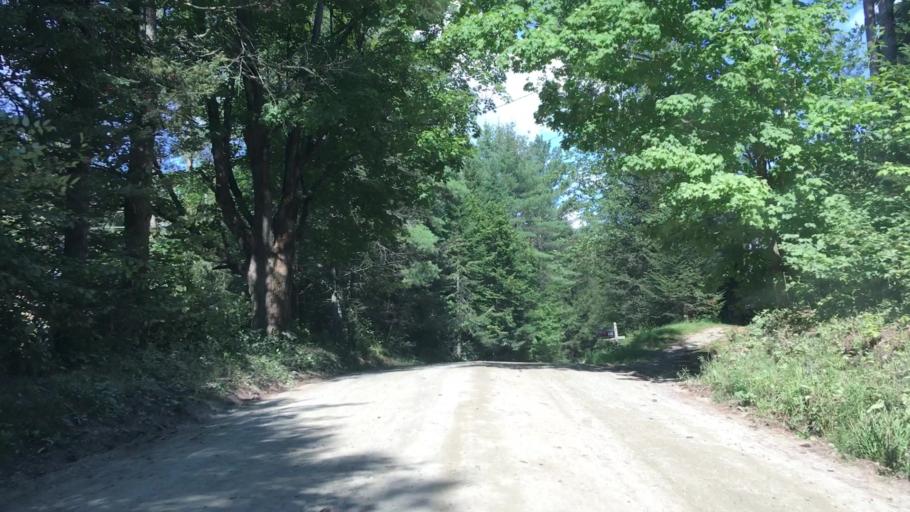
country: US
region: New Hampshire
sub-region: Grafton County
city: North Haverhill
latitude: 44.1302
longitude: -71.9615
